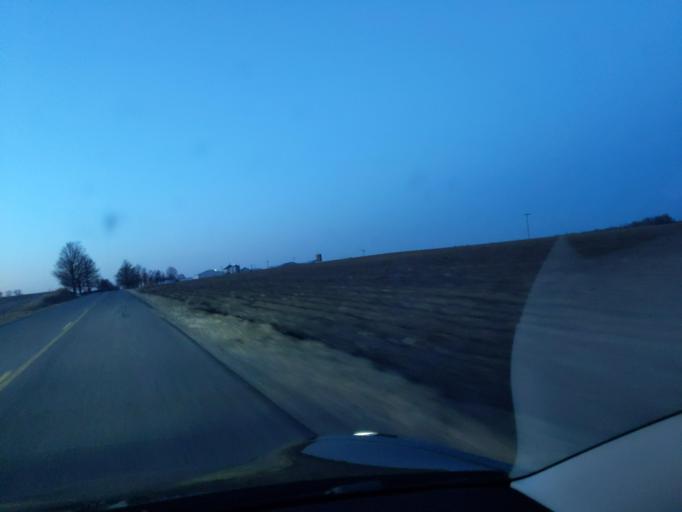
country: US
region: Michigan
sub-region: Ingham County
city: Stockbridge
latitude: 42.5206
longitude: -84.2200
